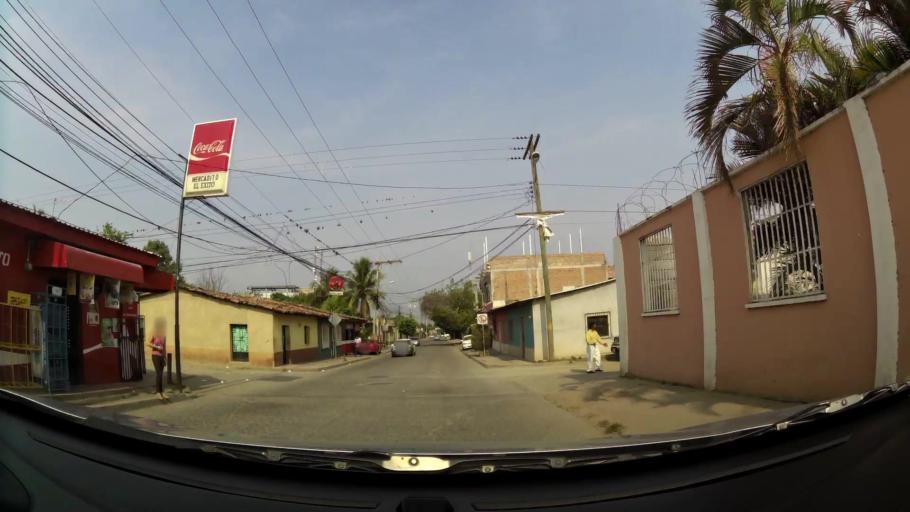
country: HN
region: Comayagua
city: Comayagua
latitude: 14.4568
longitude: -87.6321
